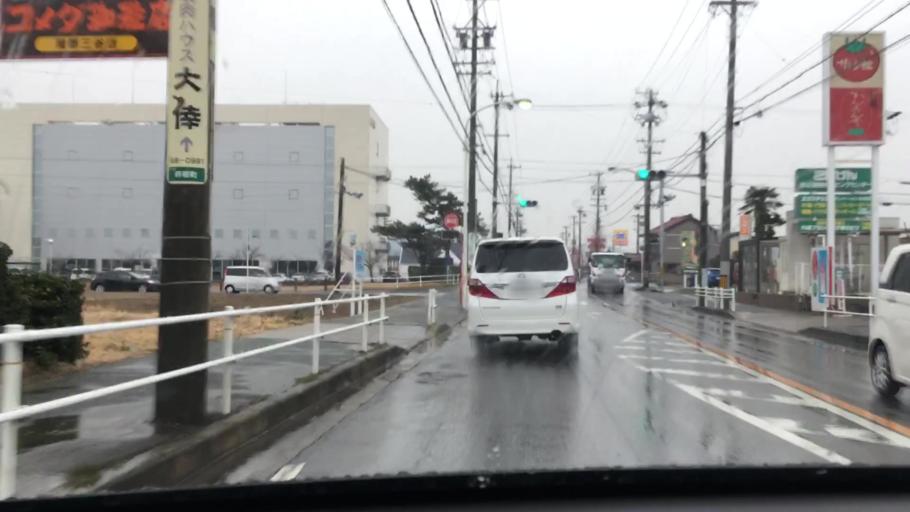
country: JP
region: Aichi
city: Gamagori
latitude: 34.8220
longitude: 137.2376
